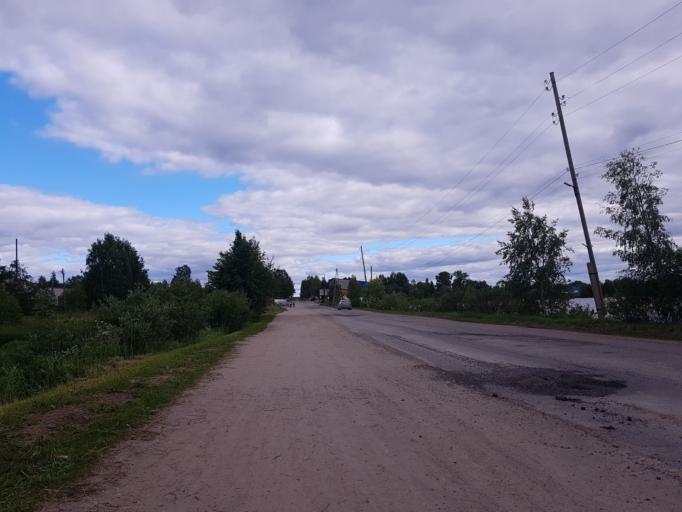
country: RU
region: Republic of Karelia
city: Kalevala
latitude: 65.2002
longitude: 31.1780
